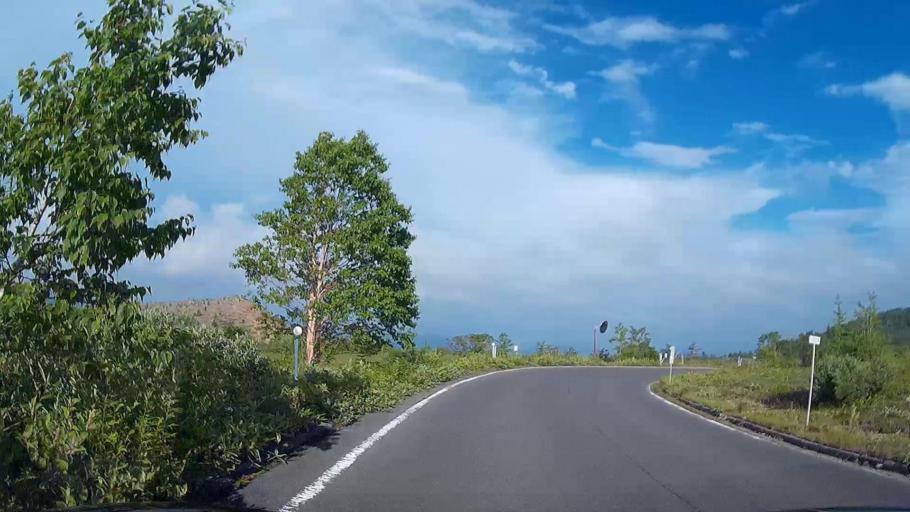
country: JP
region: Nagano
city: Nakano
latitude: 36.6371
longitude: 138.5391
